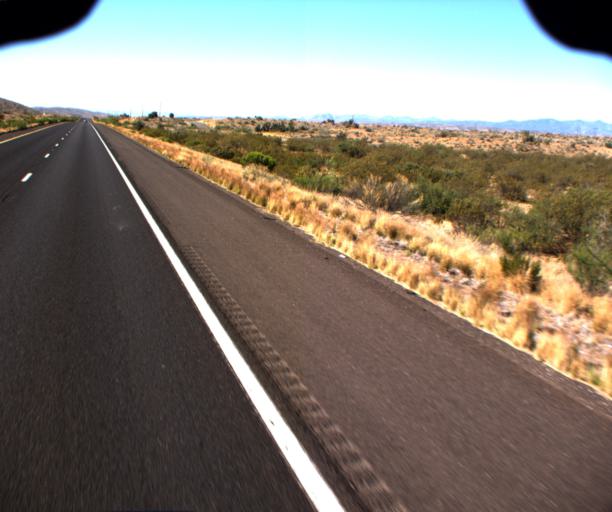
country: US
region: Arizona
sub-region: Mohave County
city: Kingman
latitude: 35.0365
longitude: -113.6651
